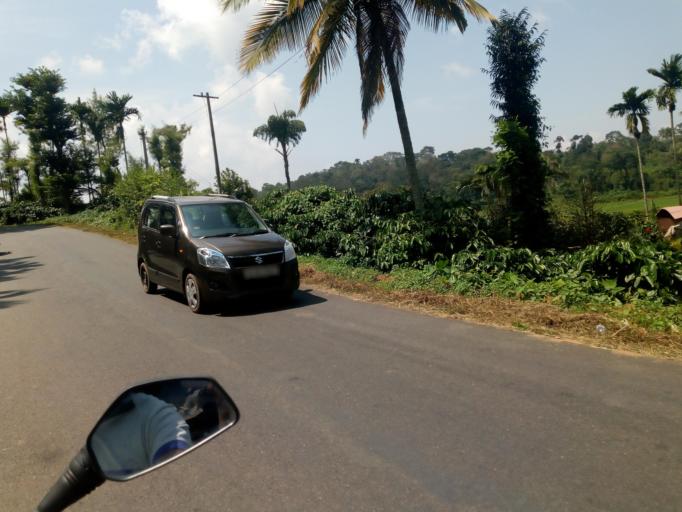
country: IN
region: Karnataka
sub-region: Kodagu
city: Ponnampet
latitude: 12.0743
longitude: 75.9425
